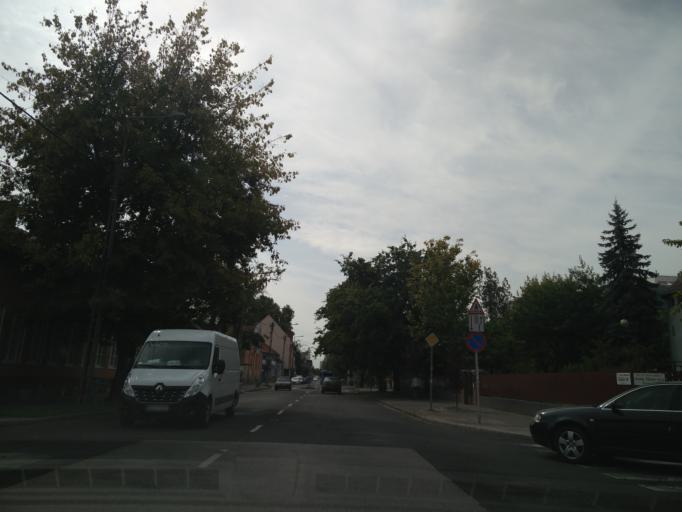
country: HU
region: Budapest
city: Budapest XV. keruelet
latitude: 47.5543
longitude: 19.1189
